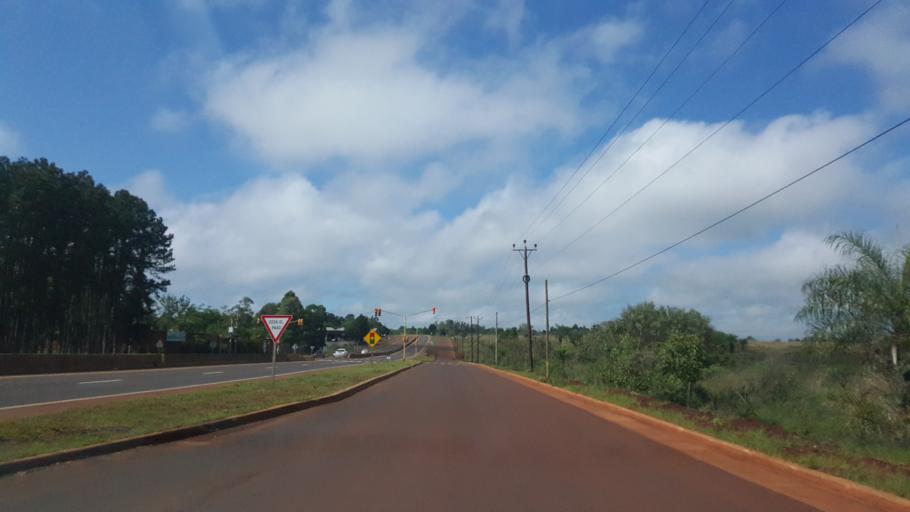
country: AR
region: Misiones
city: Garupa
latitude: -27.4859
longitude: -55.8643
